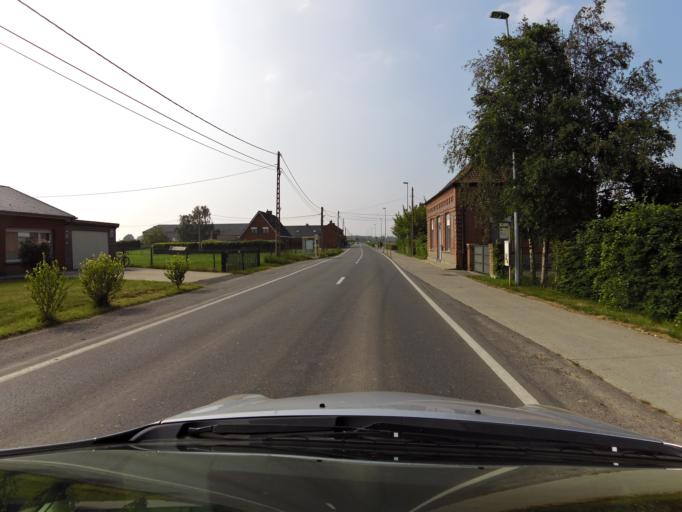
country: BE
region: Flanders
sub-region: Provincie West-Vlaanderen
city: Poperinge
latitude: 50.8707
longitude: 2.7113
